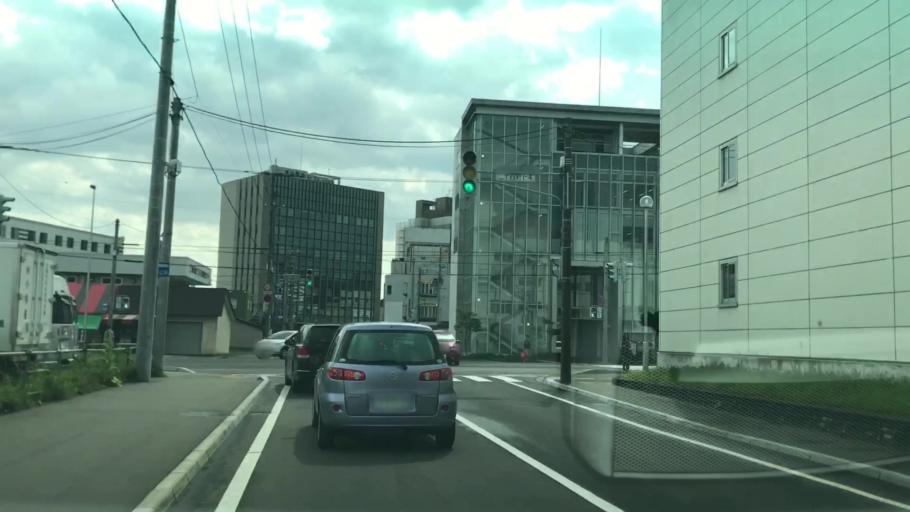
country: JP
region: Hokkaido
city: Sapporo
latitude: 43.0704
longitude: 141.3169
